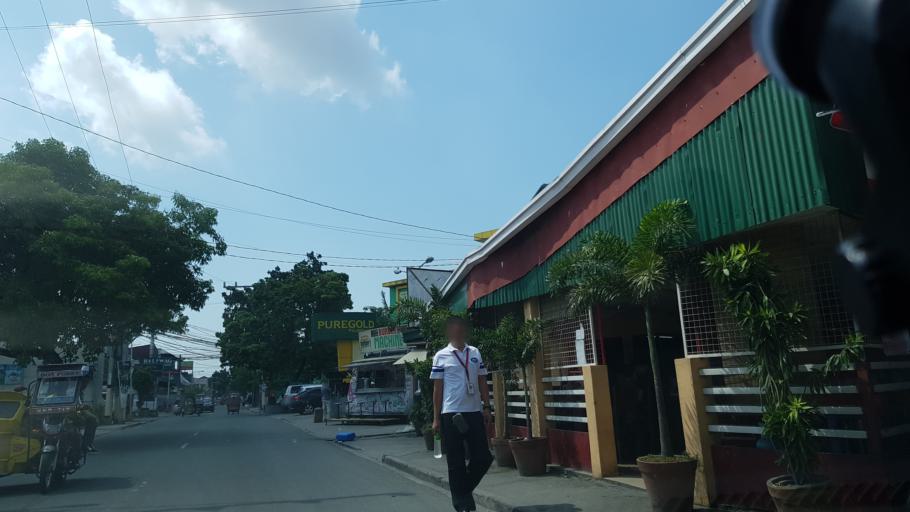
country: PH
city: Sambayanihan People's Village
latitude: 14.4630
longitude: 120.9893
